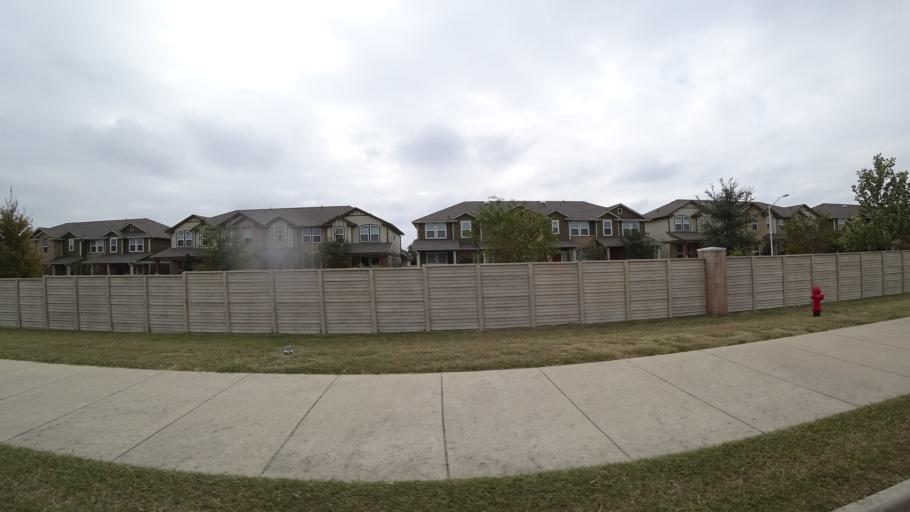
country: US
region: Texas
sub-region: Williamson County
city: Cedar Park
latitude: 30.5371
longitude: -97.8224
